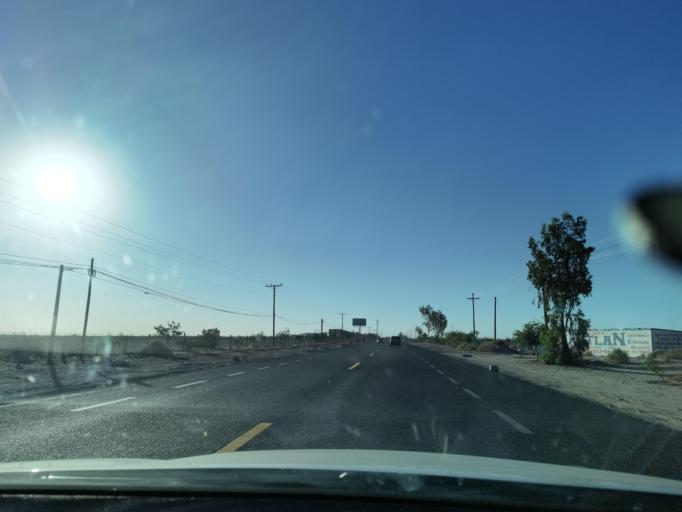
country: MX
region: Baja California
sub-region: Mexicali
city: Islas Agrarias Grupo A
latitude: 32.6322
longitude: -115.2659
